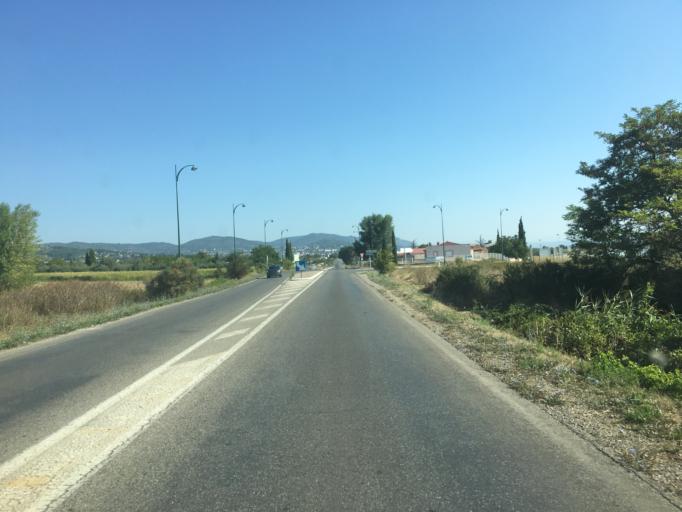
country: FR
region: Provence-Alpes-Cote d'Azur
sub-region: Departement des Alpes-de-Haute-Provence
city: Sainte-Tulle
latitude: 43.7919
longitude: 5.7731
